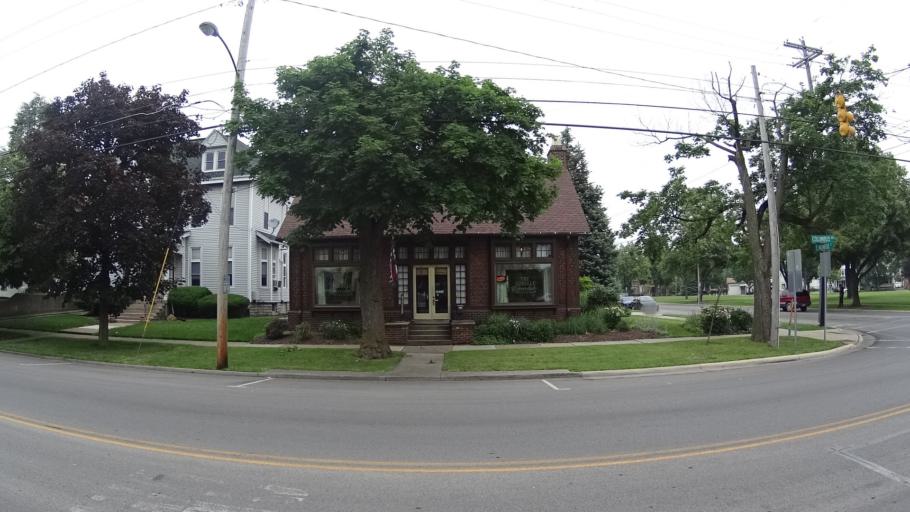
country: US
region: Ohio
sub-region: Erie County
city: Sandusky
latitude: 41.4504
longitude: -82.7084
